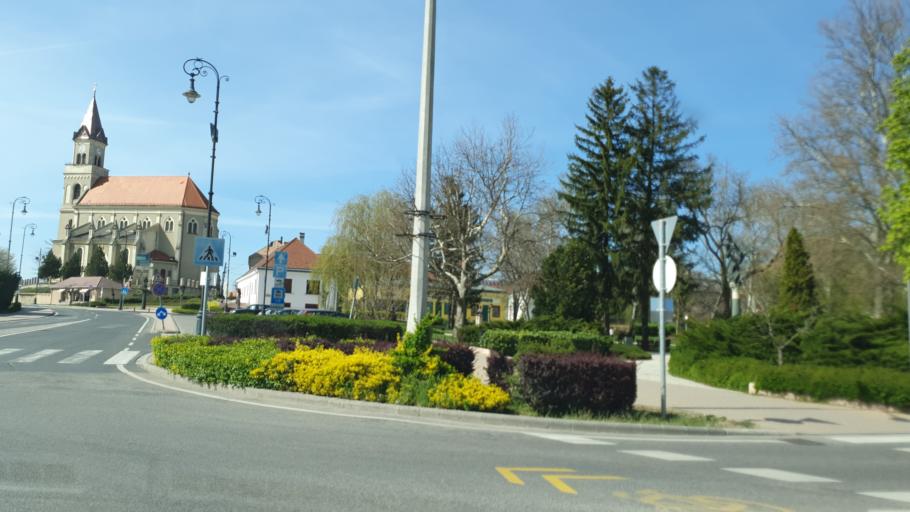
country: HU
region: Fejer
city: Mor
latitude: 47.3720
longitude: 18.2092
